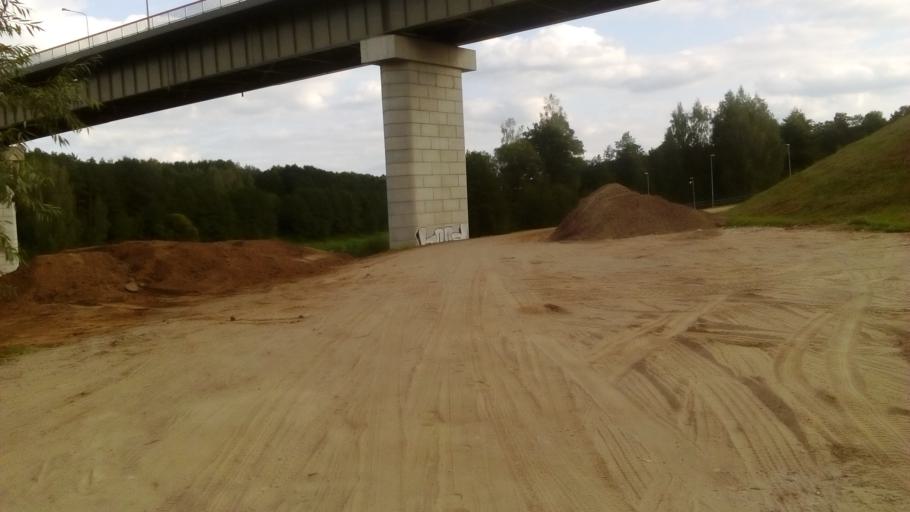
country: LT
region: Alytaus apskritis
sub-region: Alytus
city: Alytus
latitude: 54.4219
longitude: 24.0388
